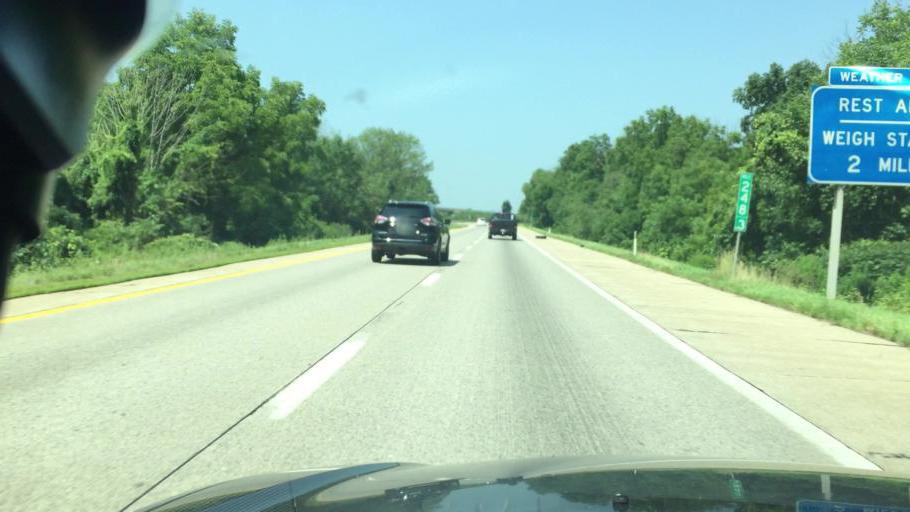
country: US
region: Pennsylvania
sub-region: Luzerne County
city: Nescopeck
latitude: 41.0173
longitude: -76.2036
